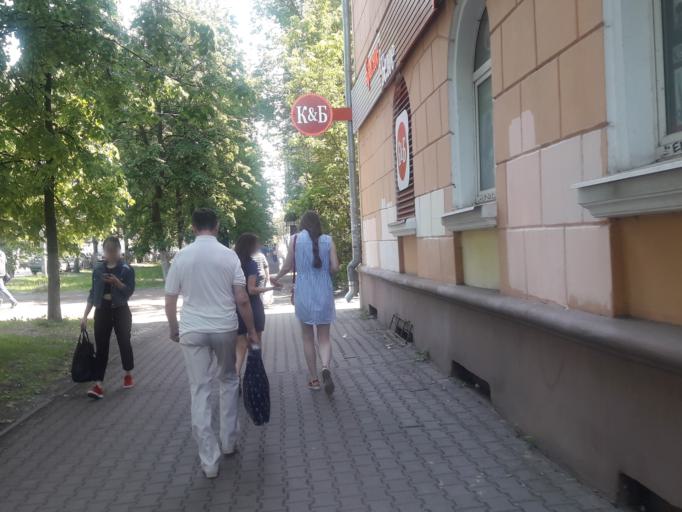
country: RU
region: Jaroslavl
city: Yaroslavl
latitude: 57.6268
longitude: 39.8458
